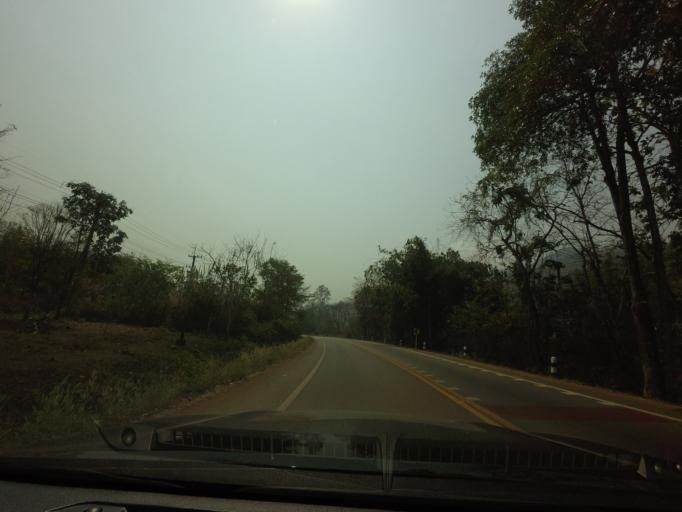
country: TH
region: Kanchanaburi
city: Thong Pha Phum
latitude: 14.7414
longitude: 98.6272
